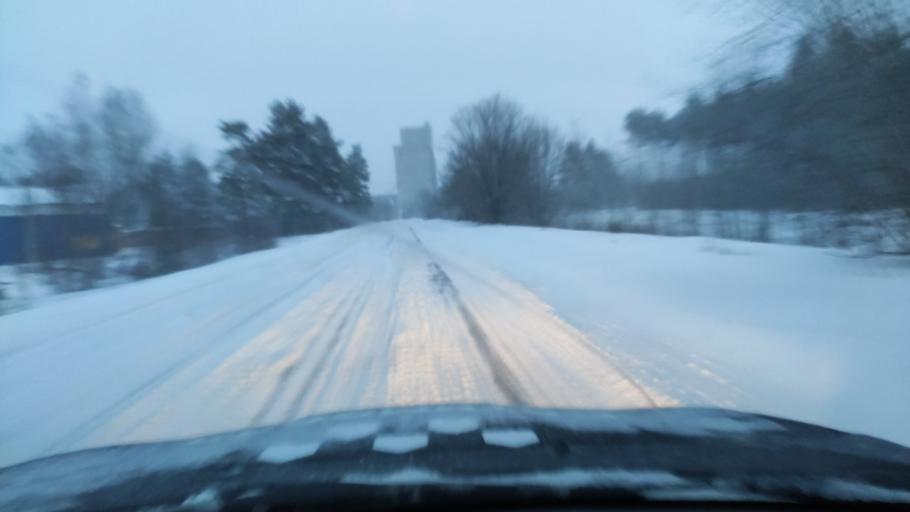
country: RU
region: Samara
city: Povolzhskiy
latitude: 53.5715
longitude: 49.6759
